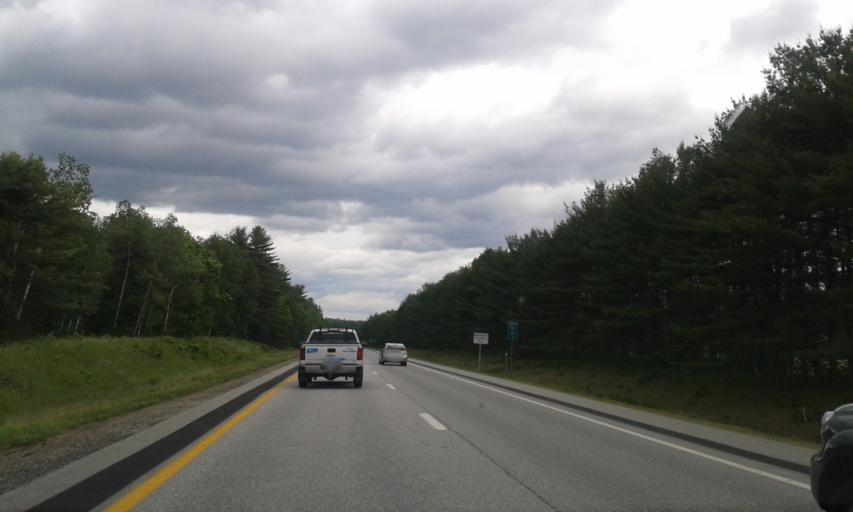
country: US
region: New Hampshire
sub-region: Merrimack County
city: Boscawen
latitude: 43.3246
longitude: -71.5980
